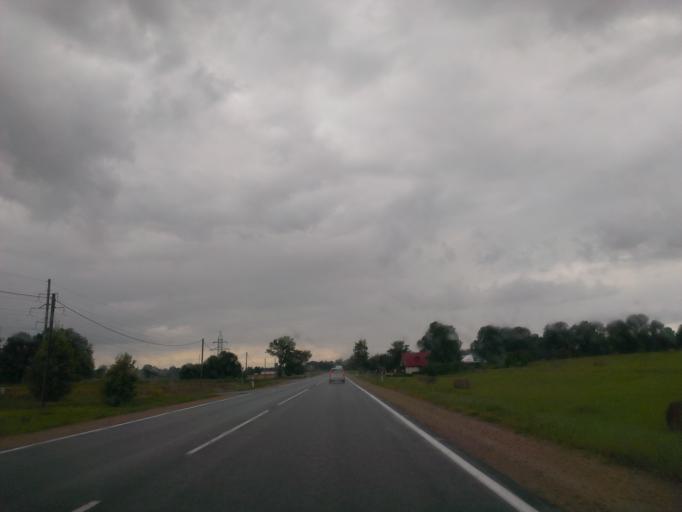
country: LV
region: Kegums
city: Kegums
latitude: 56.7630
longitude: 24.6877
